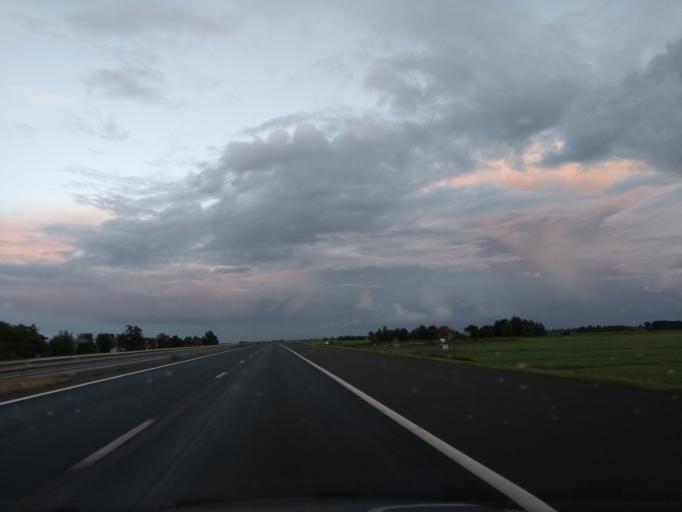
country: NL
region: Friesland
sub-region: Sudwest Fryslan
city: Oppenhuizen
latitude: 52.9945
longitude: 5.7112
